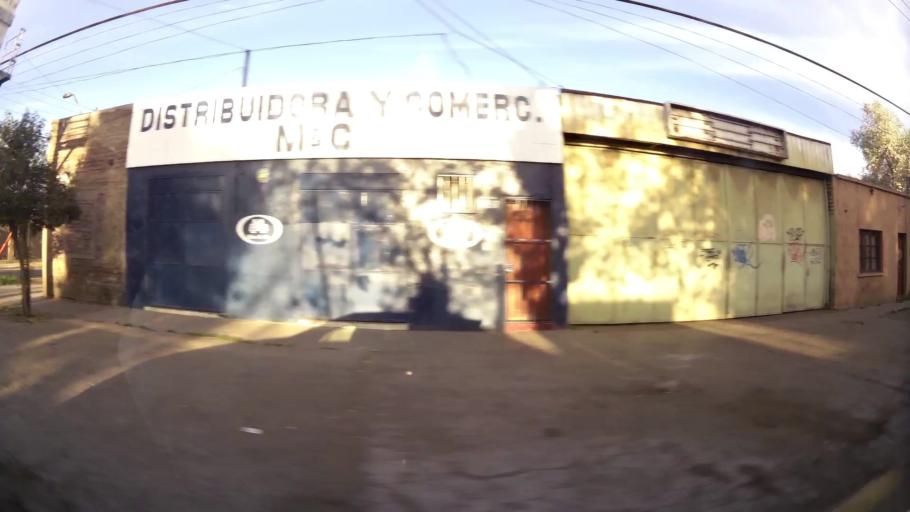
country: CL
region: Santiago Metropolitan
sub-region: Provincia de Santiago
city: Lo Prado
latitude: -33.4288
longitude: -70.7197
